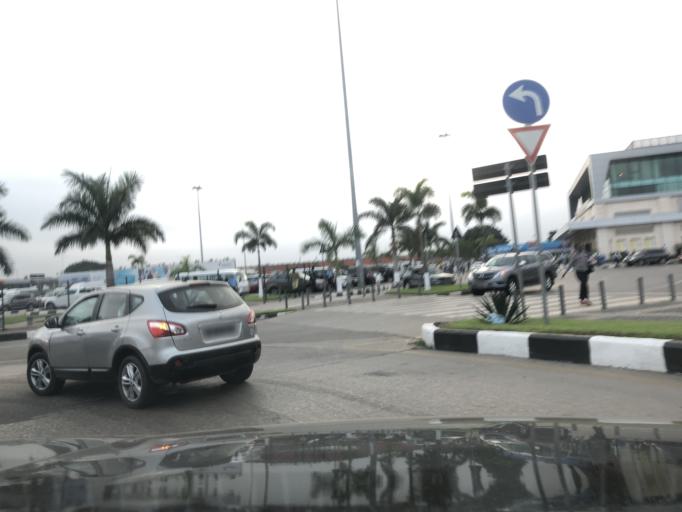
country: AO
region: Luanda
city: Luanda
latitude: -8.8470
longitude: 13.2346
